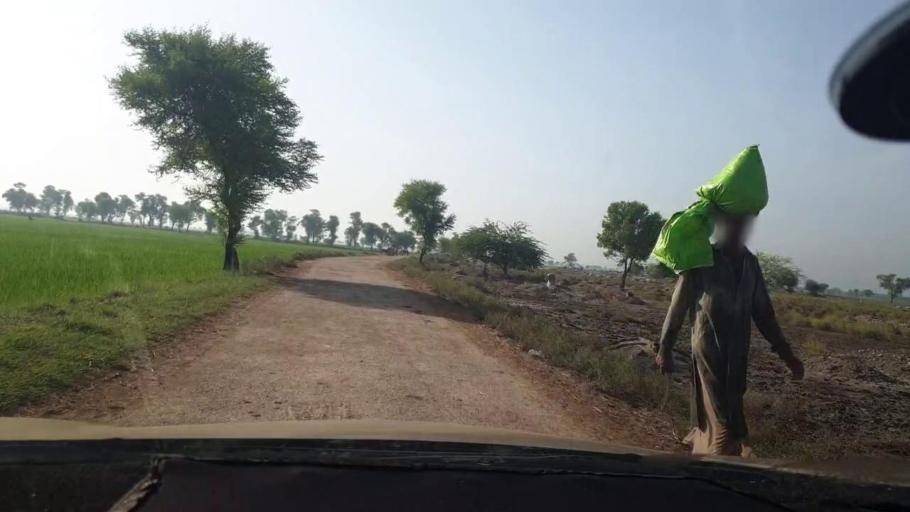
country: PK
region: Sindh
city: Kambar
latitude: 27.6442
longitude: 68.0426
